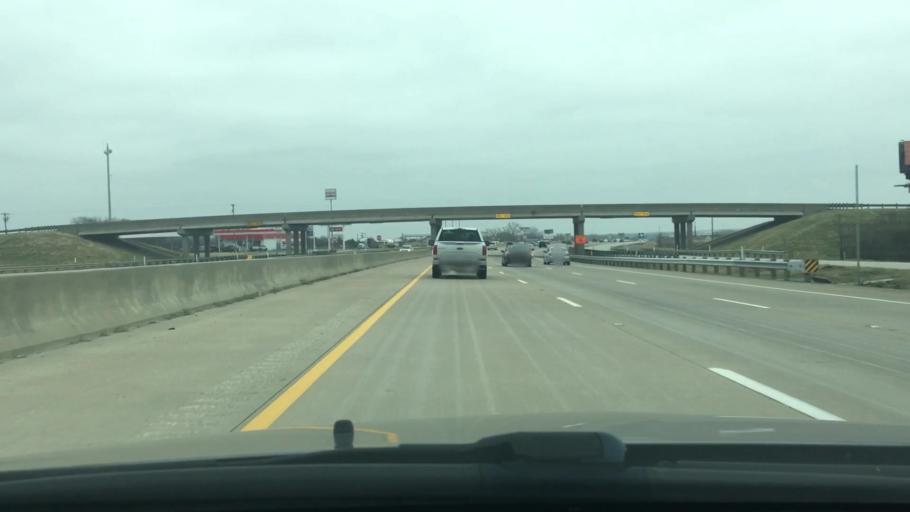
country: US
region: Texas
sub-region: Navarro County
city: Corsicana
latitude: 32.2011
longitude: -96.4747
